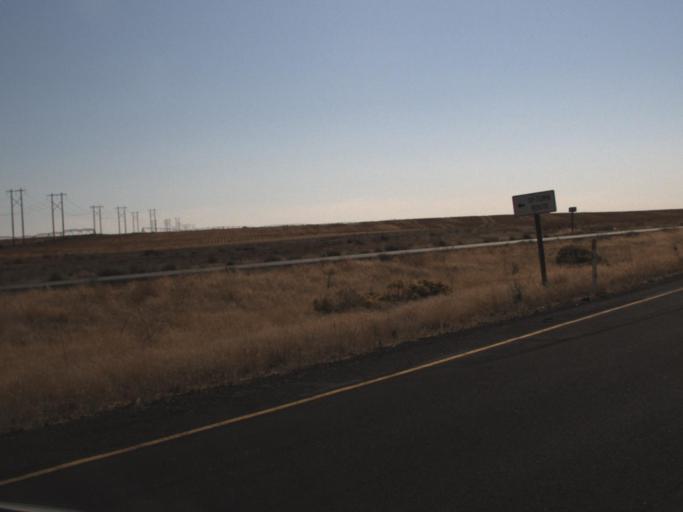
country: US
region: Washington
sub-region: Franklin County
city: Pasco
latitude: 46.3080
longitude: -119.0935
